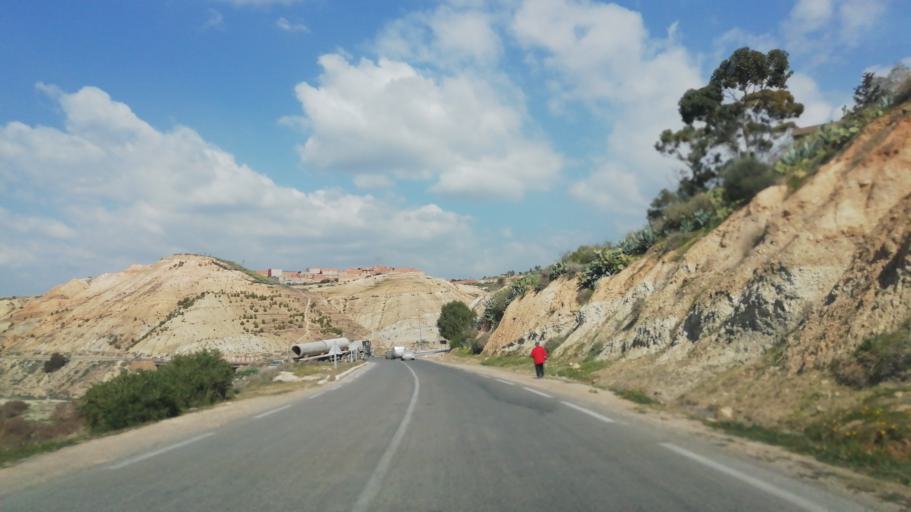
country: DZ
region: Mascara
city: Mascara
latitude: 35.5634
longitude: 0.0713
